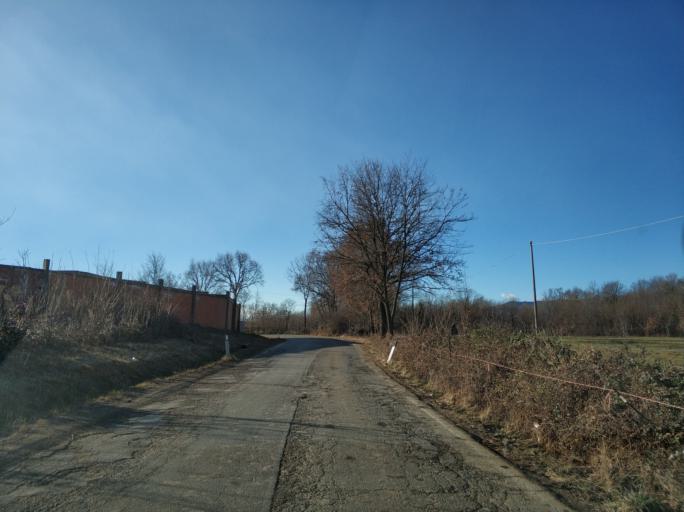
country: IT
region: Piedmont
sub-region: Provincia di Torino
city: San Carlo Canavese
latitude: 45.2556
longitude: 7.6133
